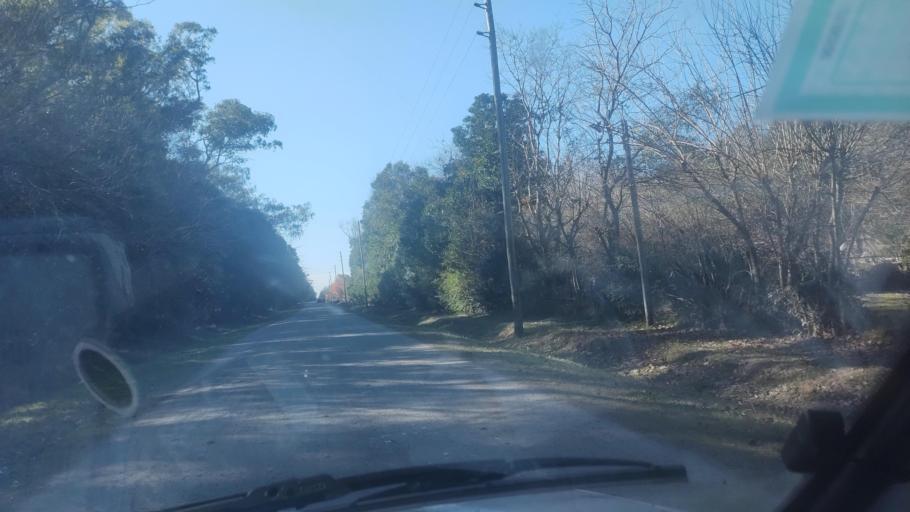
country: AR
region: Buenos Aires
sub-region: Partido de La Plata
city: La Plata
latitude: -34.8577
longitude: -58.1114
